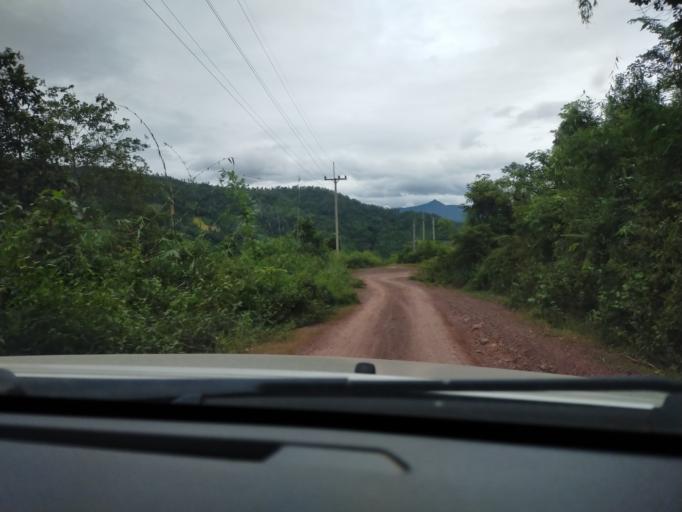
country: TH
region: Nan
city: Chaloem Phra Kiat
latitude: 19.7835
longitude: 101.3598
